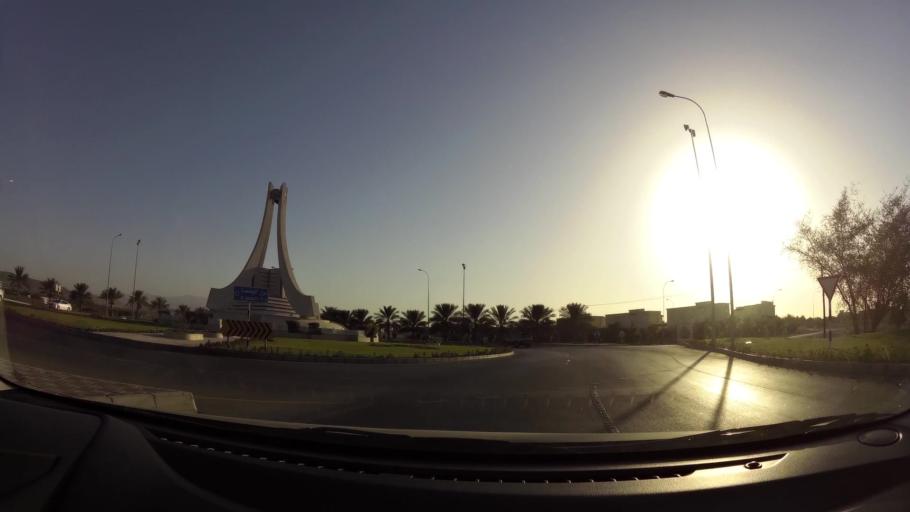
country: OM
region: Muhafazat Masqat
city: As Sib al Jadidah
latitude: 23.6068
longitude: 58.1654
